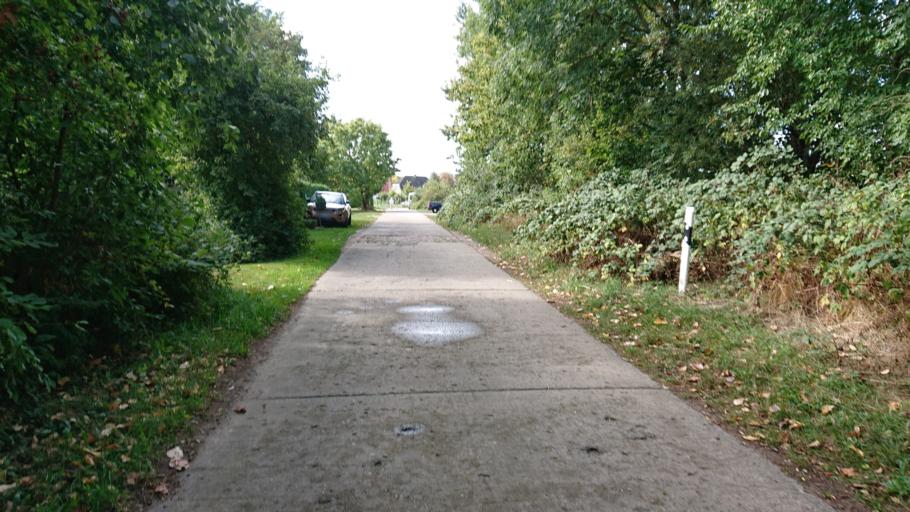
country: DE
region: Mecklenburg-Vorpommern
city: Altefahr
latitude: 54.3329
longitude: 13.1277
